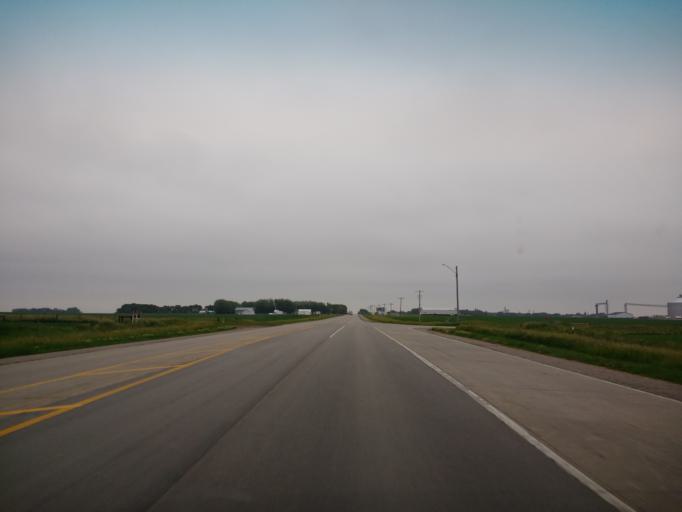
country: US
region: Iowa
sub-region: O'Brien County
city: Hartley
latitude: 43.1850
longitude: -95.5066
